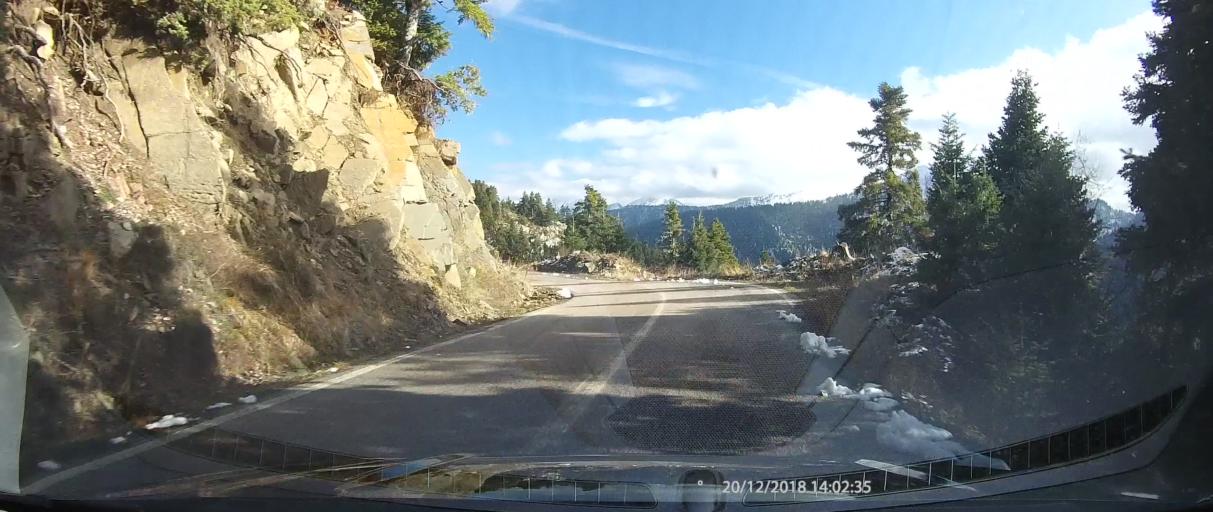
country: GR
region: West Greece
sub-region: Nomos Aitolias kai Akarnanias
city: Thermo
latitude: 38.7379
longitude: 21.6370
